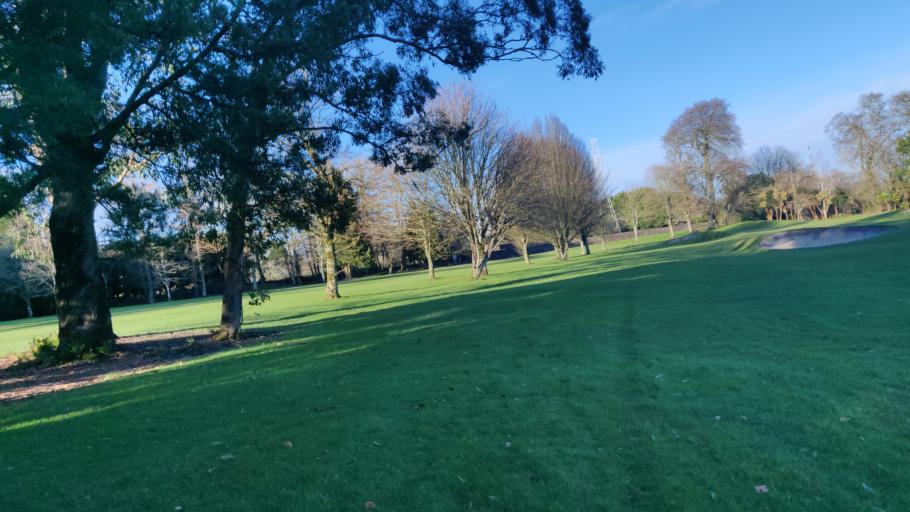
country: IE
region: Munster
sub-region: County Cork
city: Passage West
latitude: 51.8490
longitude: -8.3438
